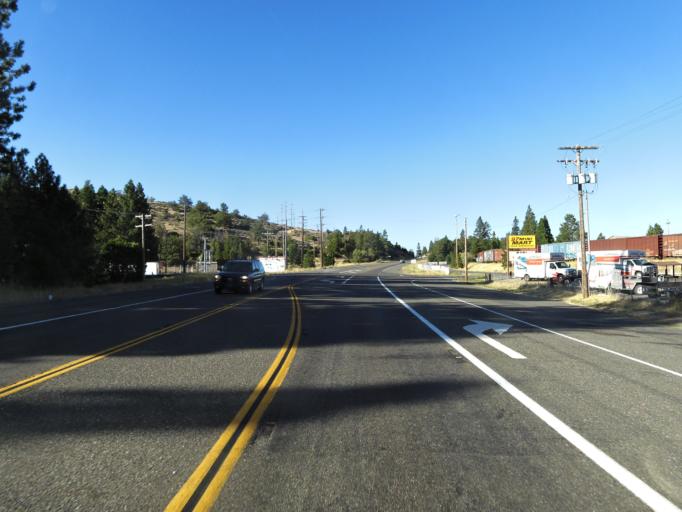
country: US
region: California
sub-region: Siskiyou County
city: Weed
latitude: 41.4298
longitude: -122.3892
